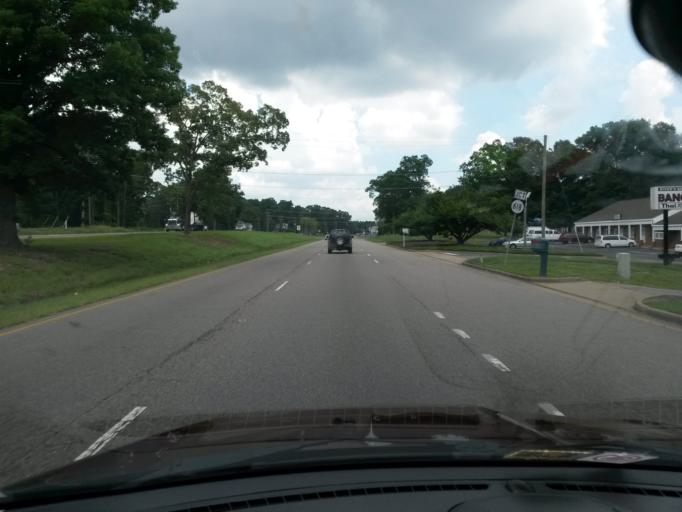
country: US
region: Virginia
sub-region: Chesterfield County
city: Enon
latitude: 37.3492
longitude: -77.3636
